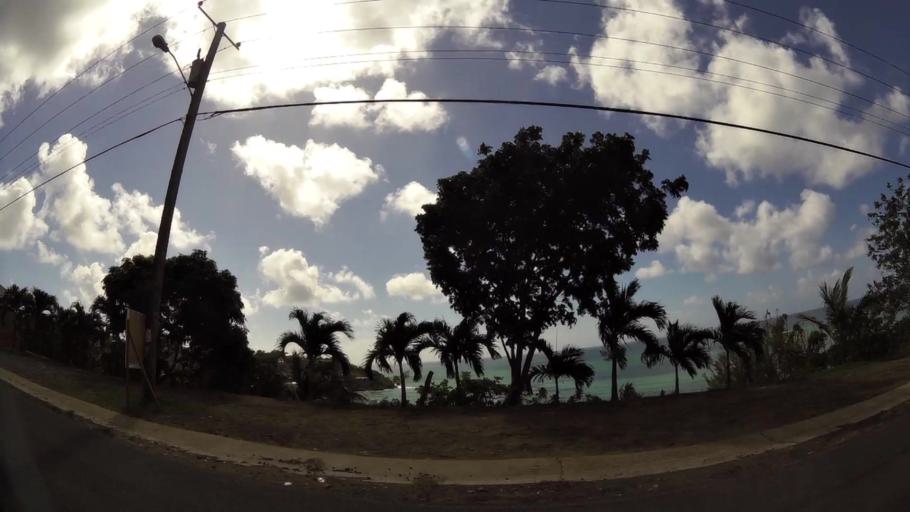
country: LC
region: Laborie Quarter
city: Laborie
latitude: 13.7538
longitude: -60.9982
